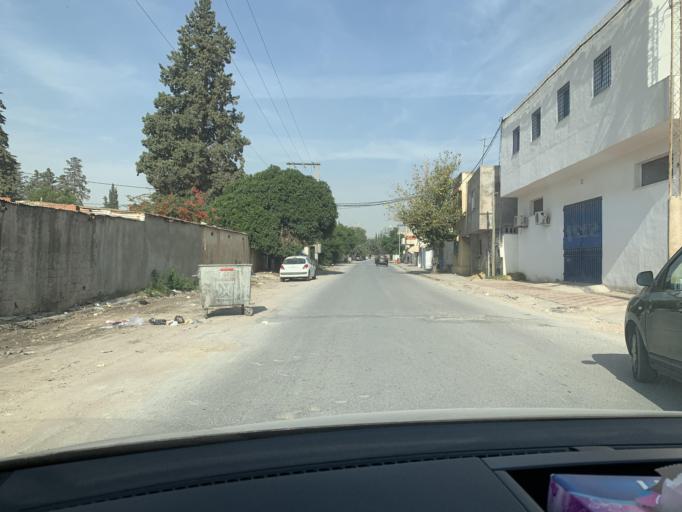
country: TN
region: Manouba
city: Manouba
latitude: 36.8138
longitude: 10.1171
